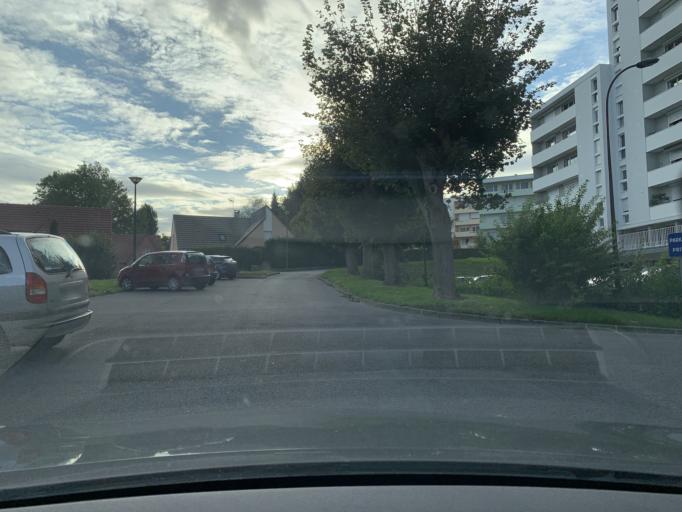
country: FR
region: Picardie
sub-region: Departement de l'Aisne
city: Harly
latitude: 49.8569
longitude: 3.3086
